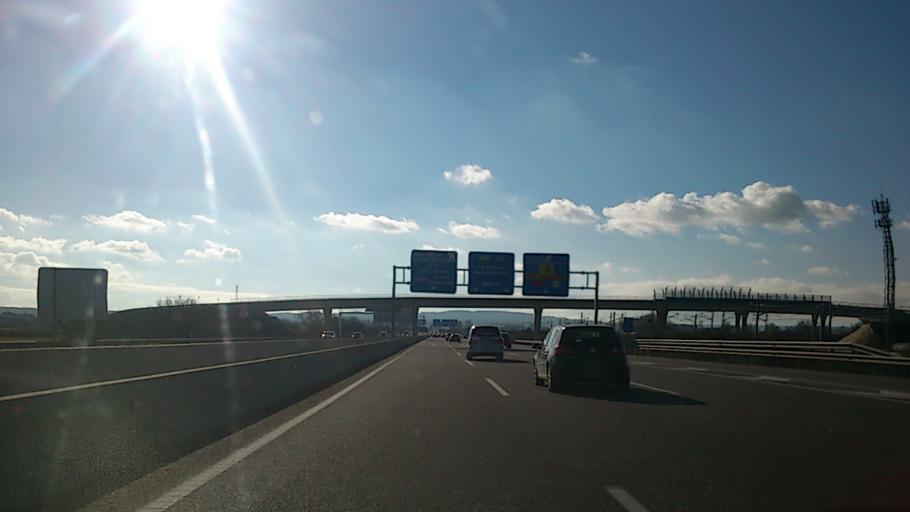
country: ES
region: Aragon
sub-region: Provincia de Zaragoza
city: Oliver-Valdefierro, Oliver, Valdefierro
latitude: 41.6543
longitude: -0.9573
